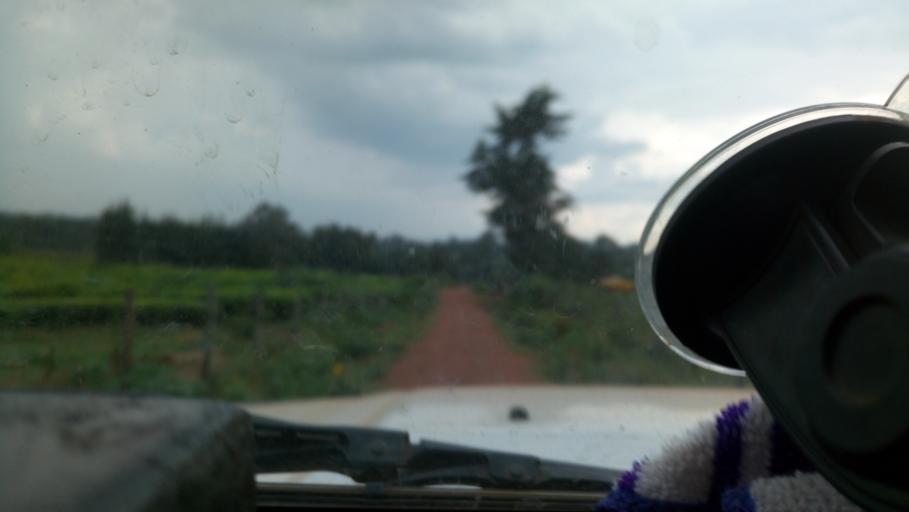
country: KE
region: Kericho
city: Litein
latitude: -0.5920
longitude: 35.1332
